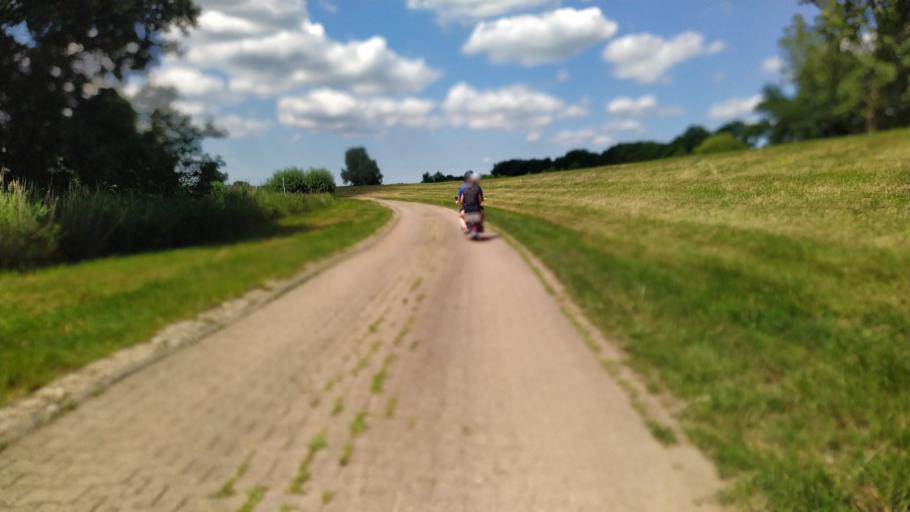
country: DE
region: Lower Saxony
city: Estorf
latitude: 53.5725
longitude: 9.1687
